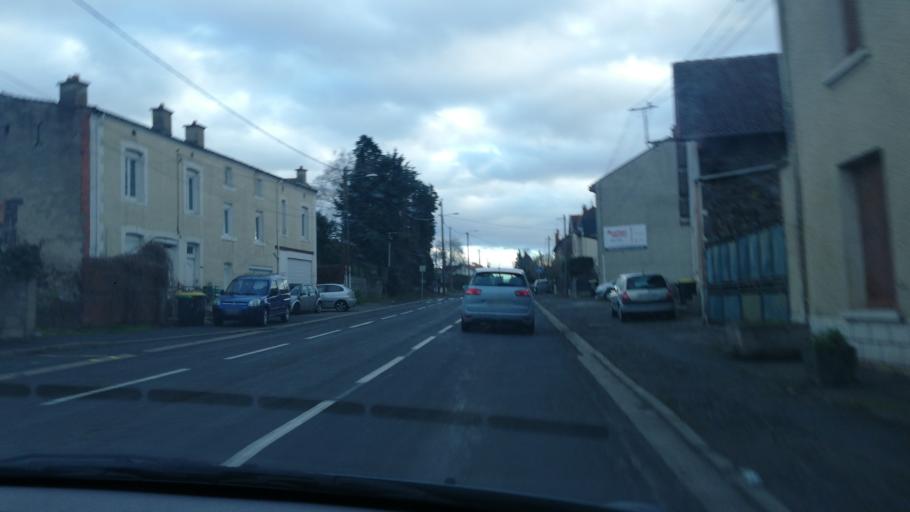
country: FR
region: Auvergne
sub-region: Departement du Puy-de-Dome
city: Vertaizon
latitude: 45.7840
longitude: 3.2875
